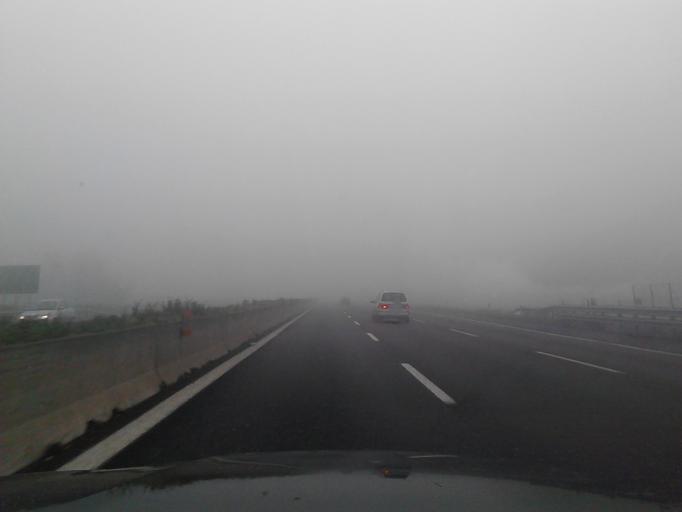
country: IT
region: Lombardy
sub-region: Provincia di Brescia
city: Capriolo
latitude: 45.6104
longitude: 9.9369
